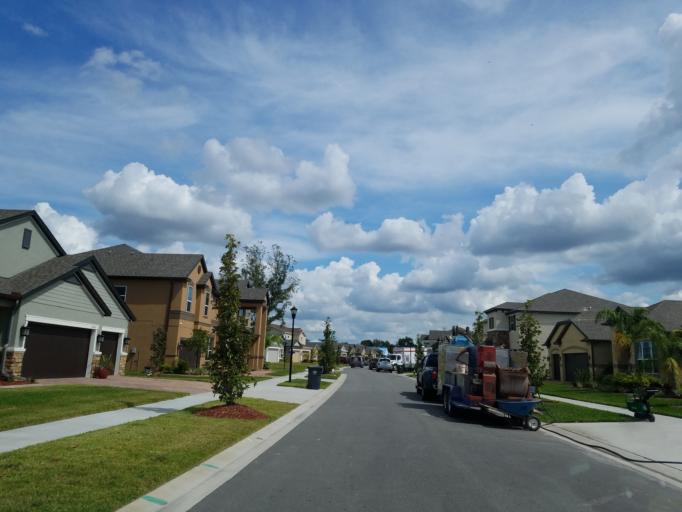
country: US
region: Florida
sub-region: Hillsborough County
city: Riverview
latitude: 27.8996
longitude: -82.3268
